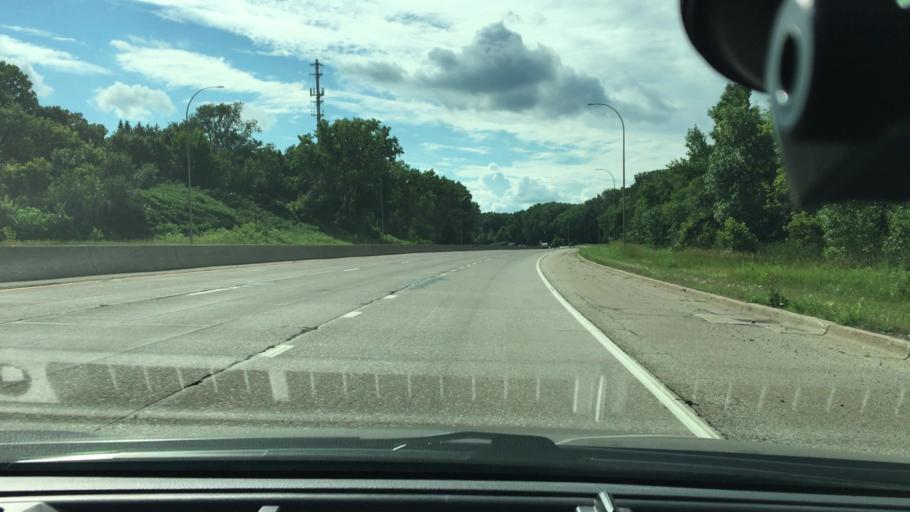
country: US
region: Minnesota
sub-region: Hennepin County
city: Wayzata
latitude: 44.9767
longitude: -93.5153
